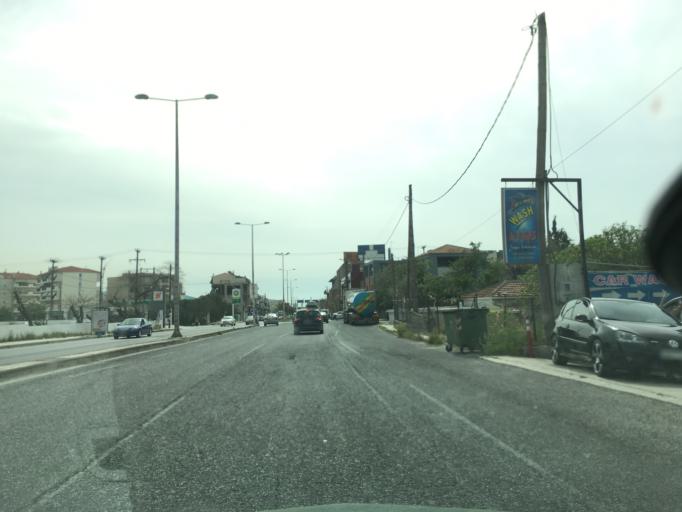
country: GR
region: Thessaly
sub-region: Nomos Magnisias
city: Nea Ionia
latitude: 39.3685
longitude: 22.9198
